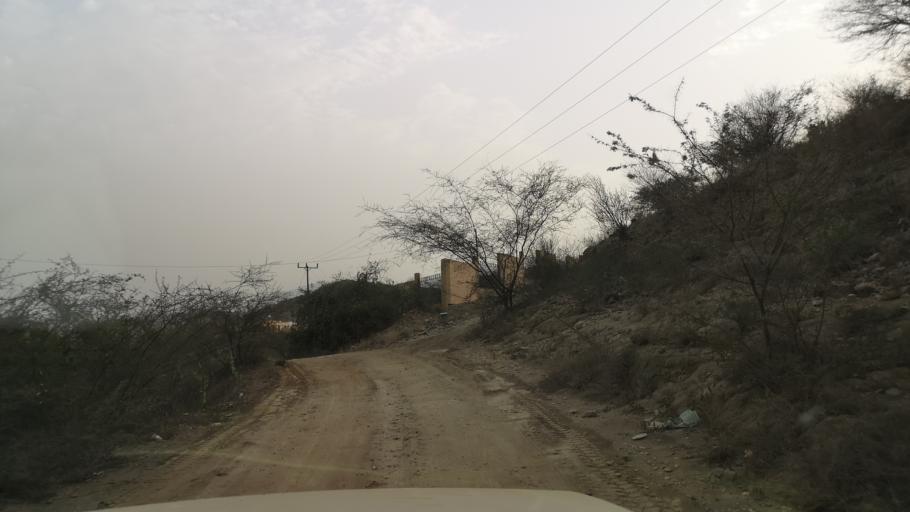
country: YE
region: Sa'dah
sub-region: Monabbih
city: Suq al Khamis
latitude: 17.3692
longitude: 43.1276
